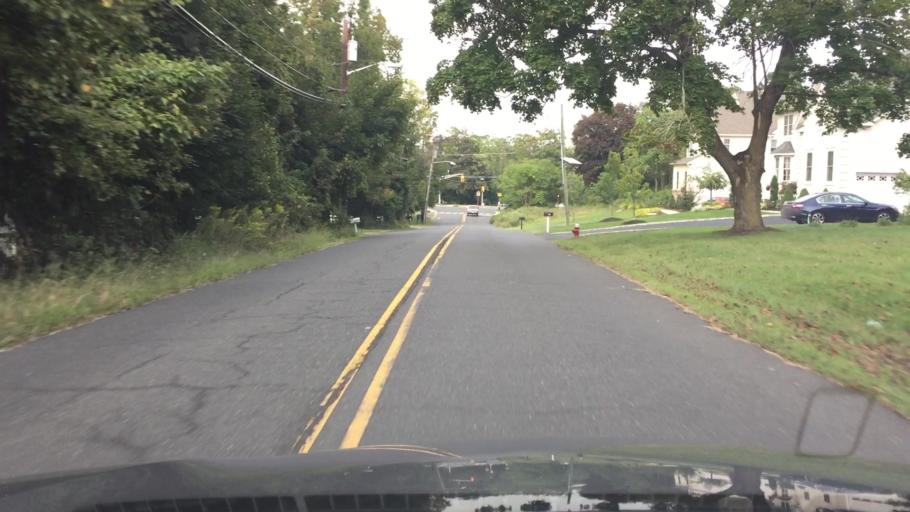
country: US
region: New Jersey
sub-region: Somerset County
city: Somerset
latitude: 40.5271
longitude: -74.4999
